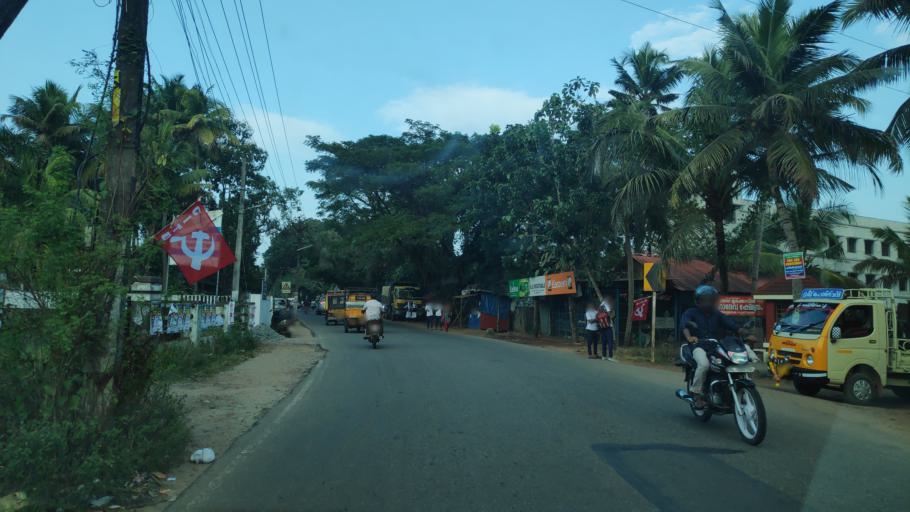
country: IN
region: Kerala
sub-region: Alappuzha
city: Alleppey
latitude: 9.5749
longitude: 76.3485
